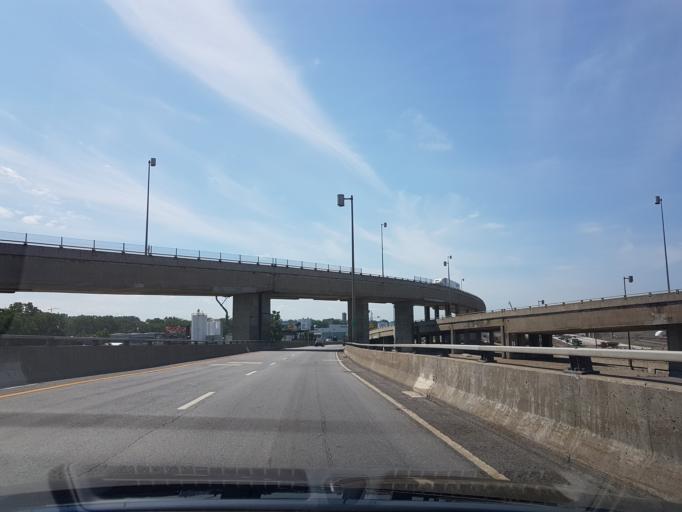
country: CA
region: Quebec
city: Saint-Raymond
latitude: 45.4671
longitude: -73.6002
